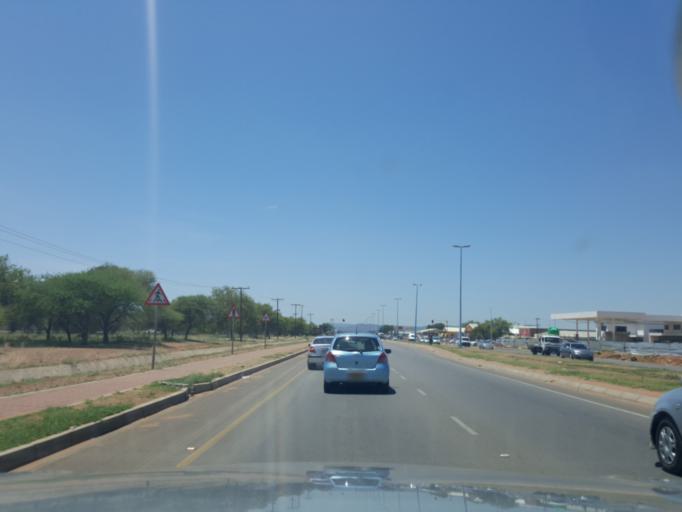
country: BW
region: Kweneng
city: Mogoditshane
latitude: -24.6104
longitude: 25.8601
